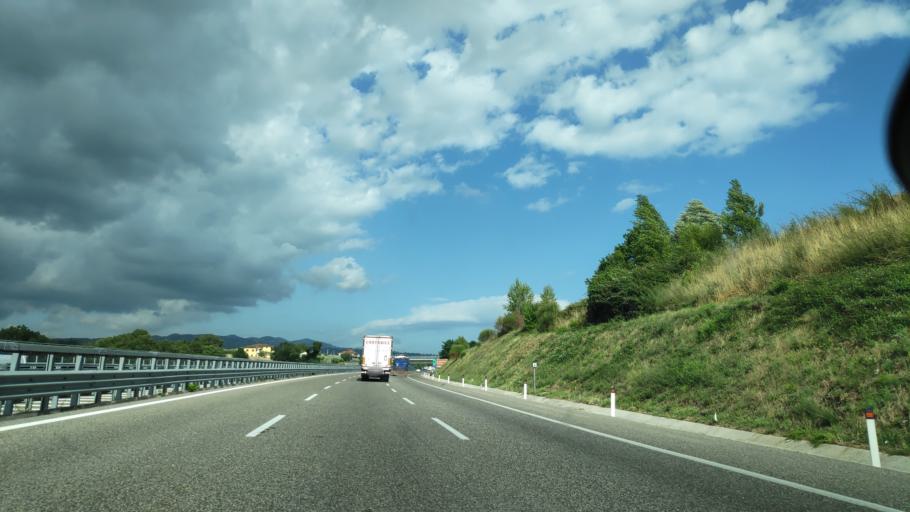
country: IT
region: Campania
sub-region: Provincia di Salerno
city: Contursi Terme
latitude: 40.6148
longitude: 15.2710
